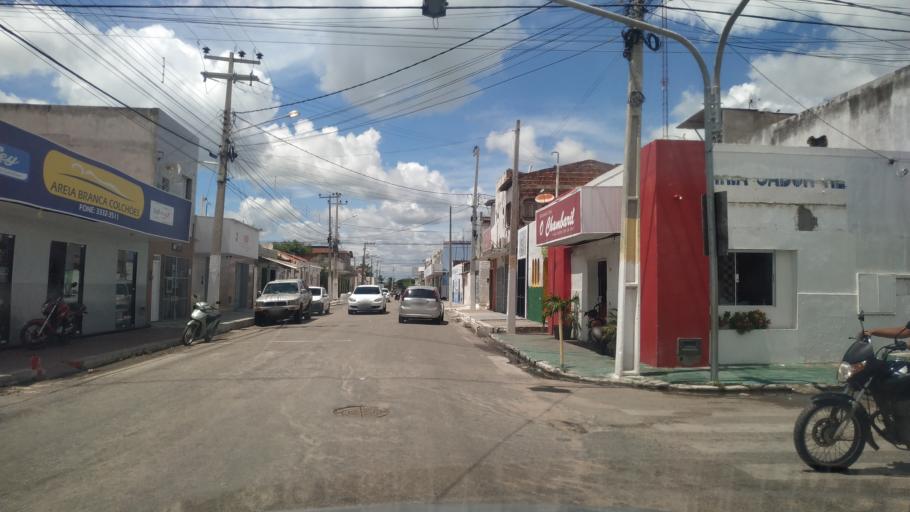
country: BR
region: Rio Grande do Norte
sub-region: Areia Branca
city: Areia Branca
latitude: -4.9546
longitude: -37.1314
